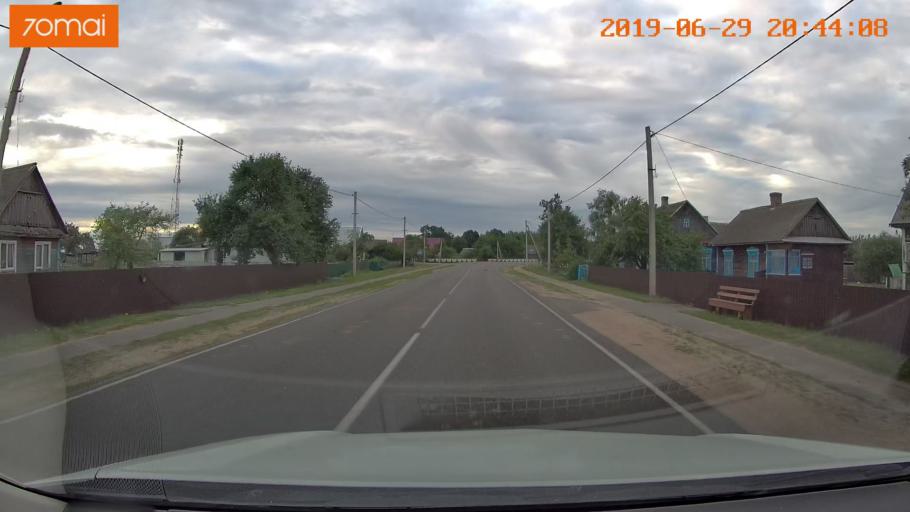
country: BY
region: Brest
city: Hantsavichy
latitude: 52.6108
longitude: 26.3084
